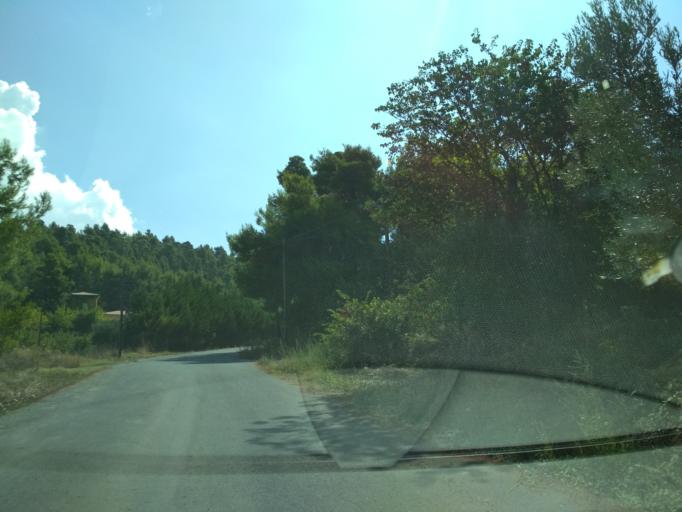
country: GR
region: Central Greece
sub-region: Nomos Evvoias
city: Roviai
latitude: 38.8191
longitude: 23.2712
